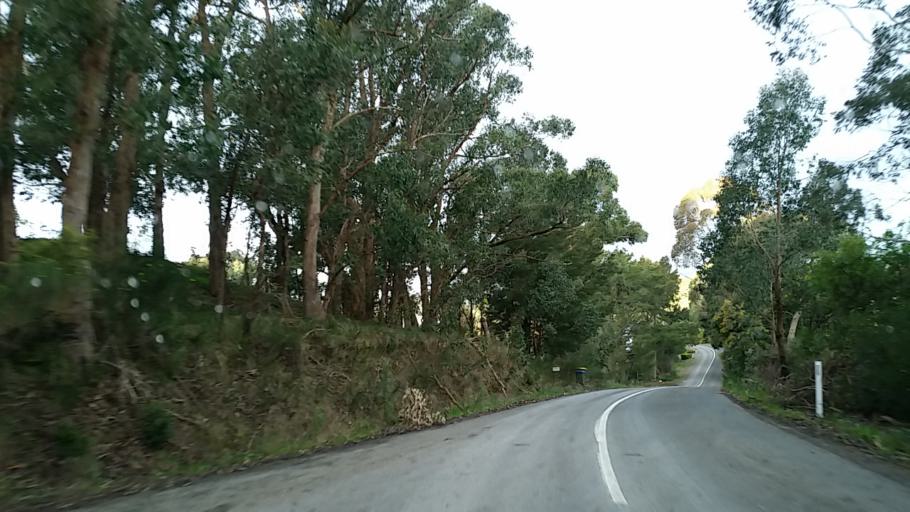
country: AU
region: South Australia
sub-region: Adelaide Hills
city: Lobethal
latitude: -34.8963
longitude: 138.8230
